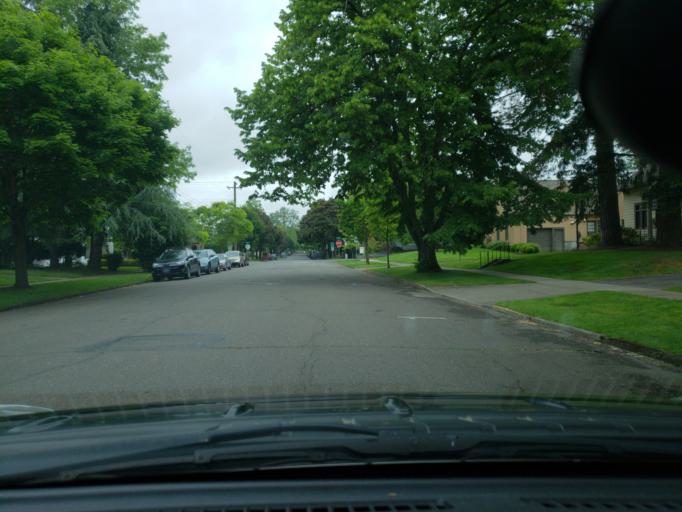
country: US
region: Oregon
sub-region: Marion County
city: Salem
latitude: 44.9465
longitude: -123.0282
